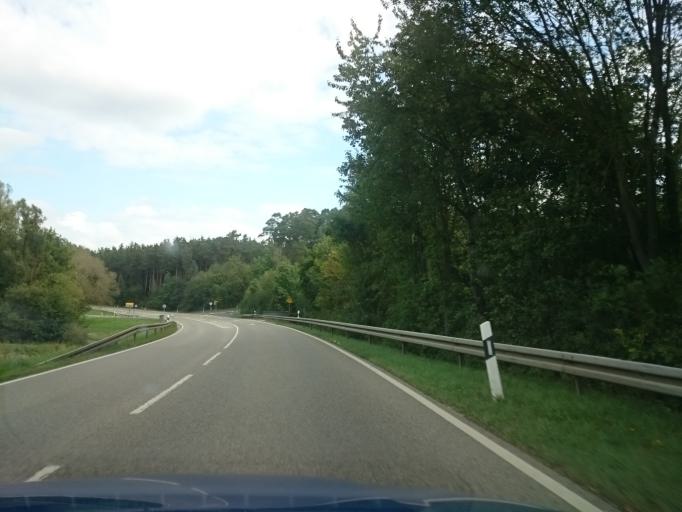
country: DE
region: Bavaria
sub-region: Regierungsbezirk Mittelfranken
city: Allersberg
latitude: 49.2392
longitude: 11.2148
